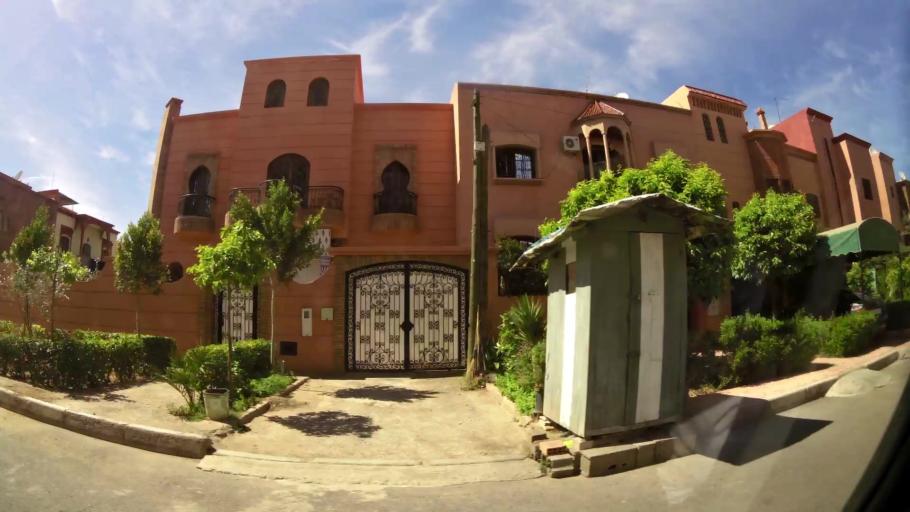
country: MA
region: Marrakech-Tensift-Al Haouz
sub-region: Marrakech
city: Marrakesh
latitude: 31.6744
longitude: -8.0016
